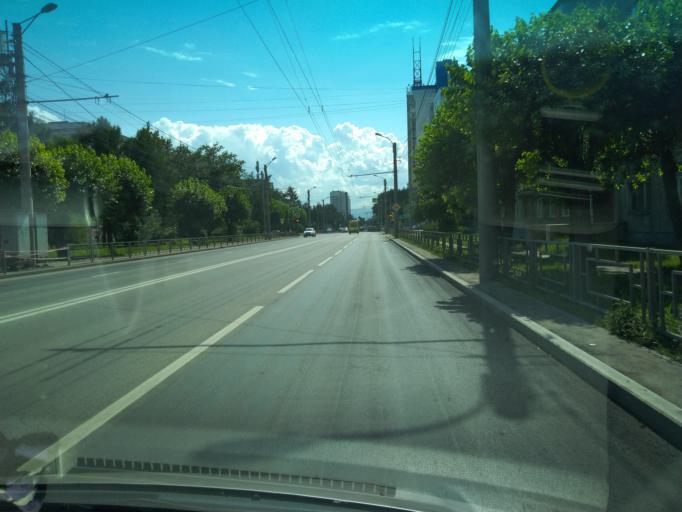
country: RU
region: Krasnoyarskiy
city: Solnechnyy
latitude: 56.0480
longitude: 92.9415
